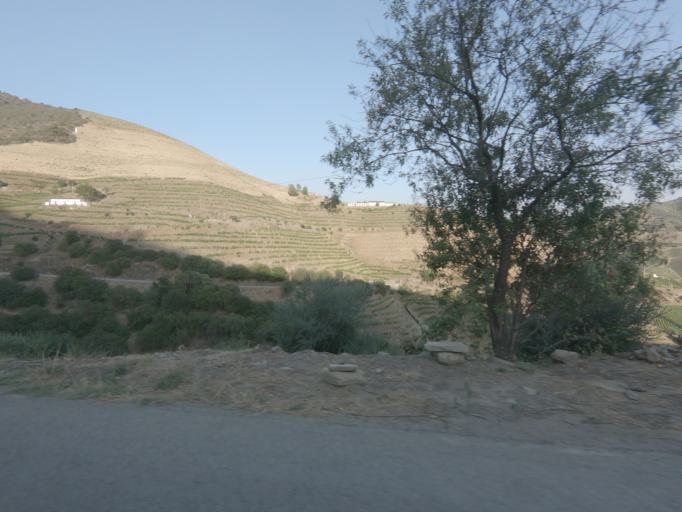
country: PT
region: Vila Real
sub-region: Sabrosa
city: Vilela
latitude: 41.1667
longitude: -7.6265
